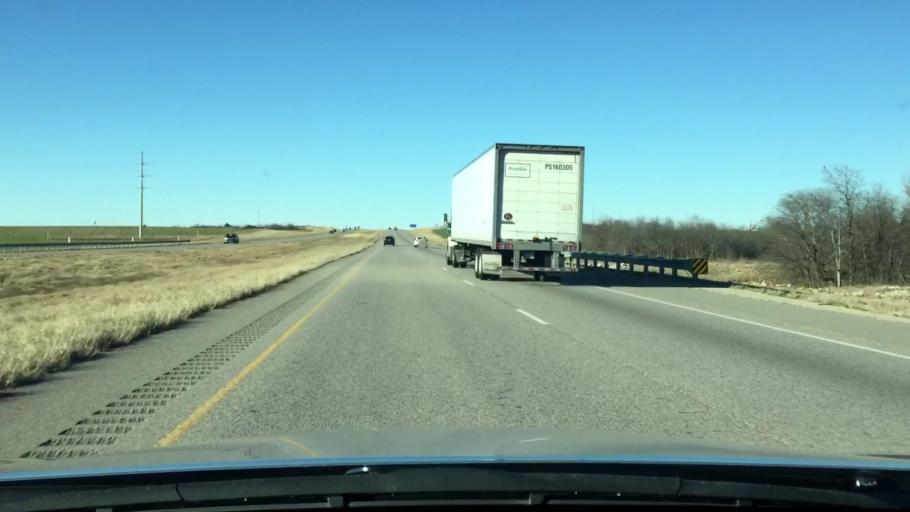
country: US
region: Texas
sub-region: Hill County
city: Itasca
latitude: 32.1343
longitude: -97.1204
